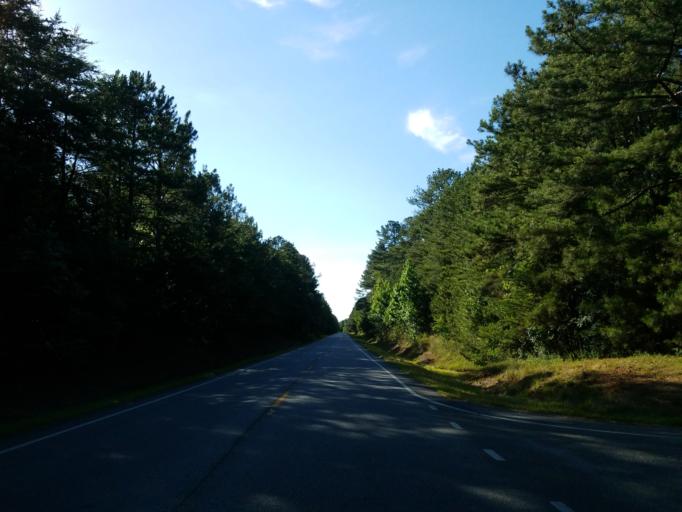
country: US
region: Georgia
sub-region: Gordon County
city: Calhoun
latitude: 34.5823
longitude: -85.0006
